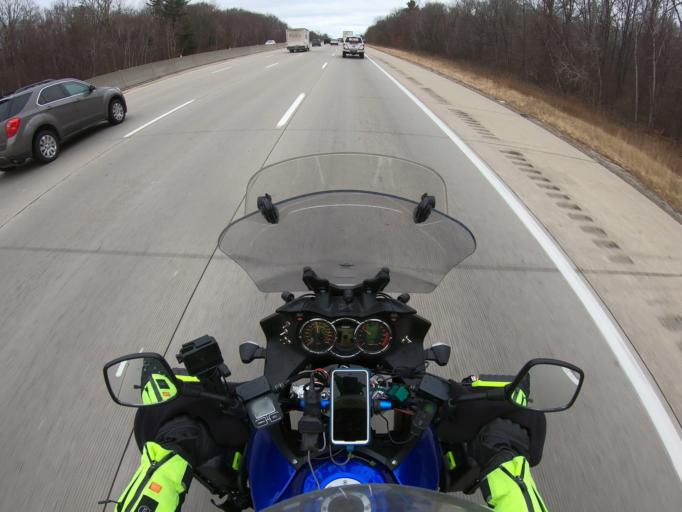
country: US
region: Michigan
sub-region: Saginaw County
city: Birch Run
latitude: 43.2866
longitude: -83.8109
